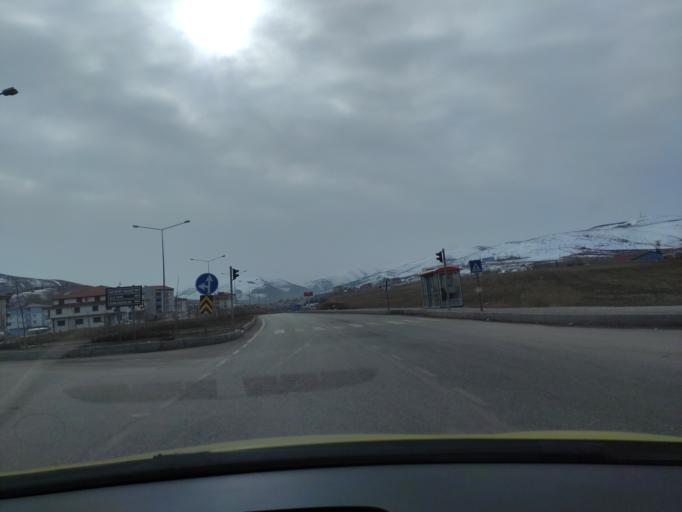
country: TR
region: Bayburt
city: Bayburt
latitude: 40.2652
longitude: 40.2041
